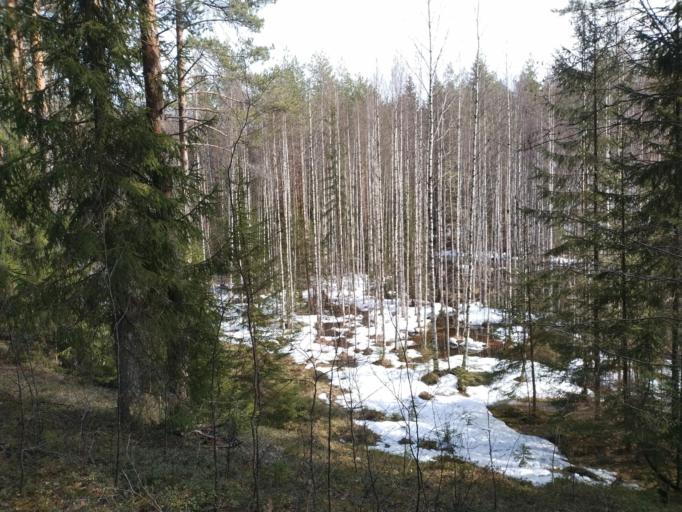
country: FI
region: Southern Savonia
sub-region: Savonlinna
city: Punkaharju
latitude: 61.6725
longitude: 29.3136
